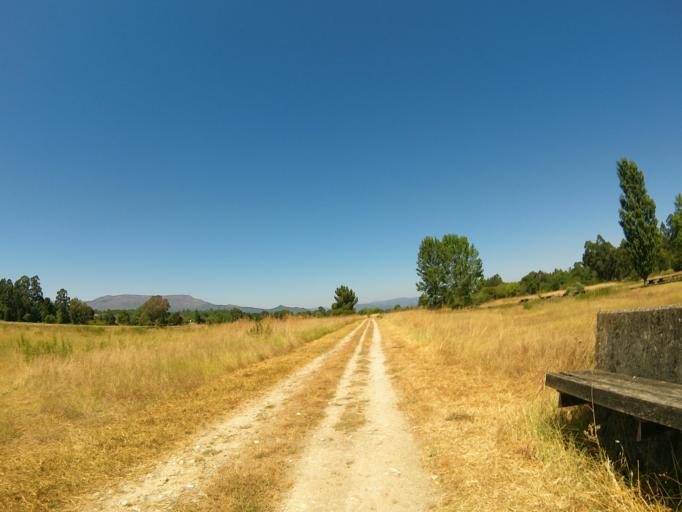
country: PT
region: Viana do Castelo
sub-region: Viana do Castelo
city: Darque
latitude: 41.7079
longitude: -8.7163
